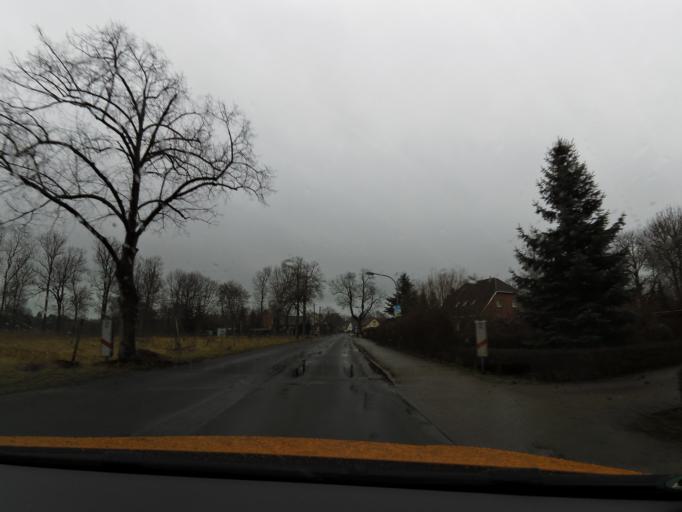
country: DE
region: Brandenburg
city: Zossen
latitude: 52.2371
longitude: 13.4390
